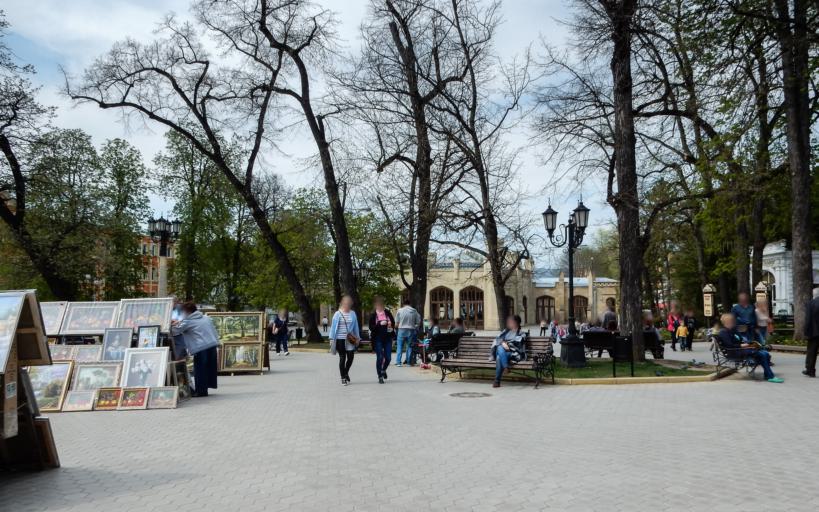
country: RU
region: Stavropol'skiy
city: Kislovodsk
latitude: 43.8989
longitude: 42.7173
